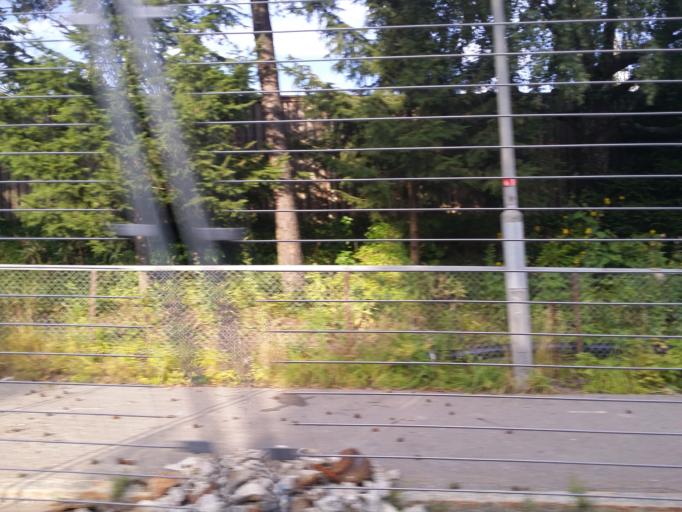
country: NO
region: Akershus
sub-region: Oppegard
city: Kolbotn
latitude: 59.8967
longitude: 10.8535
